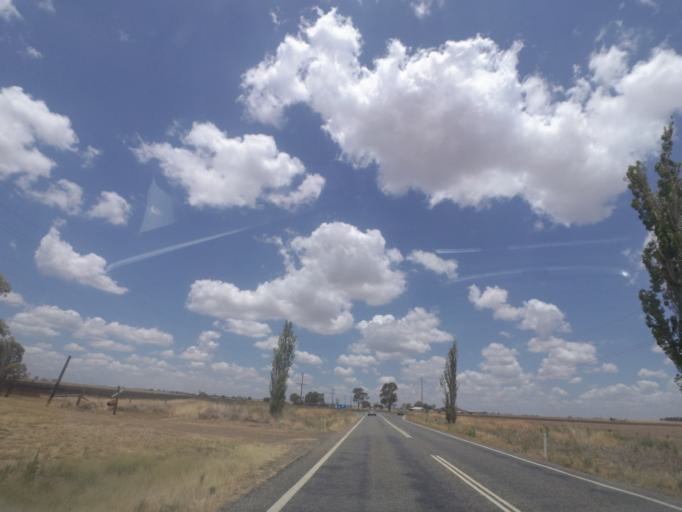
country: AU
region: Queensland
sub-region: Toowoomba
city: Top Camp
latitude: -27.9256
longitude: 151.9843
